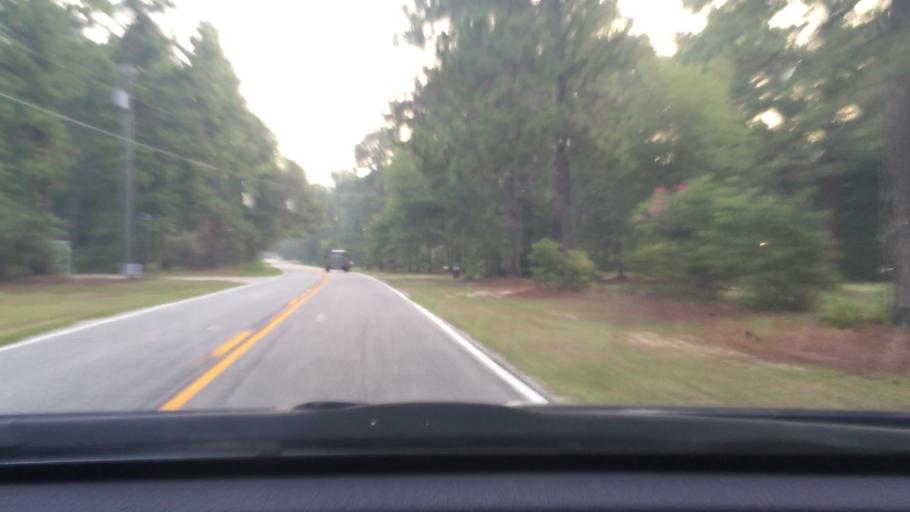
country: US
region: South Carolina
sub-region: Darlington County
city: Hartsville
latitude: 34.3304
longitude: -80.1032
